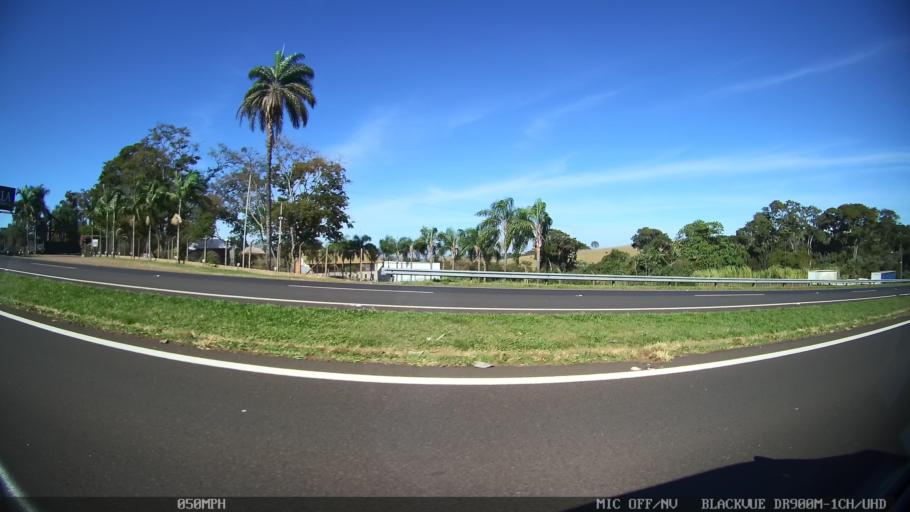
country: BR
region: Sao Paulo
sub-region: Franca
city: Franca
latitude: -20.5756
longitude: -47.3594
